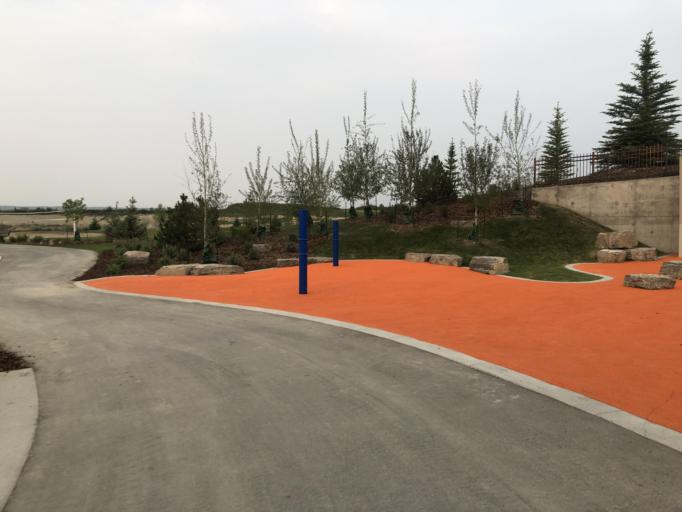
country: CA
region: Alberta
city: Cochrane
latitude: 51.1139
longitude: -114.3892
